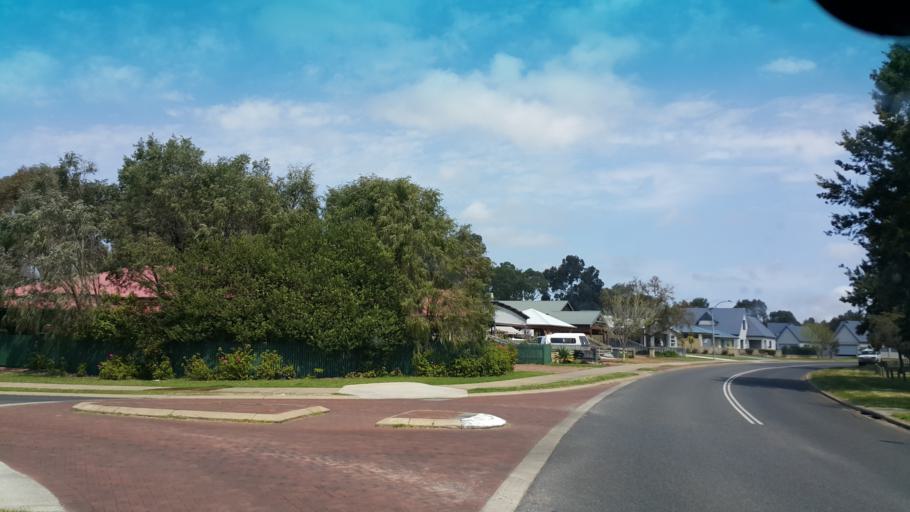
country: AU
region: Western Australia
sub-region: Busselton
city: Quindalup
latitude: -33.6226
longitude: 115.1074
